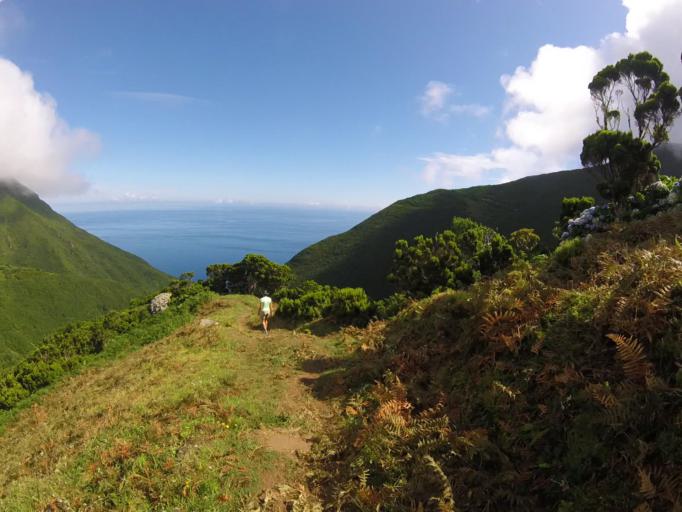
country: PT
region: Azores
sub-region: Sao Roque do Pico
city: Sao Roque do Pico
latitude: 38.6049
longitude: -27.9204
